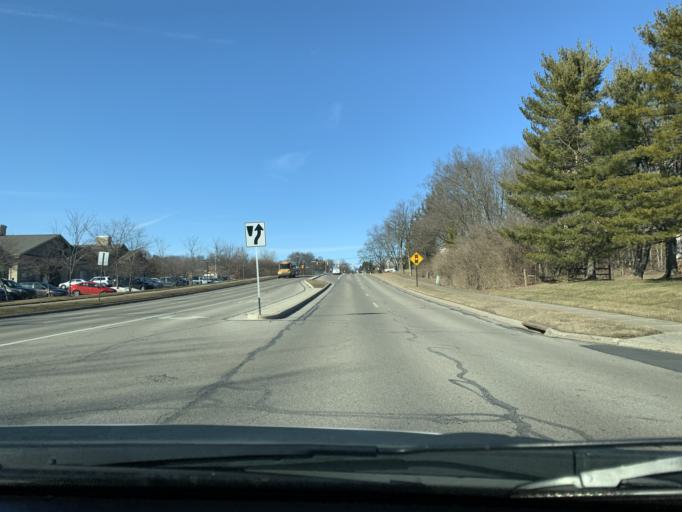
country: US
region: Ohio
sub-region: Montgomery County
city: Centerville
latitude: 39.6417
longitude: -84.1383
